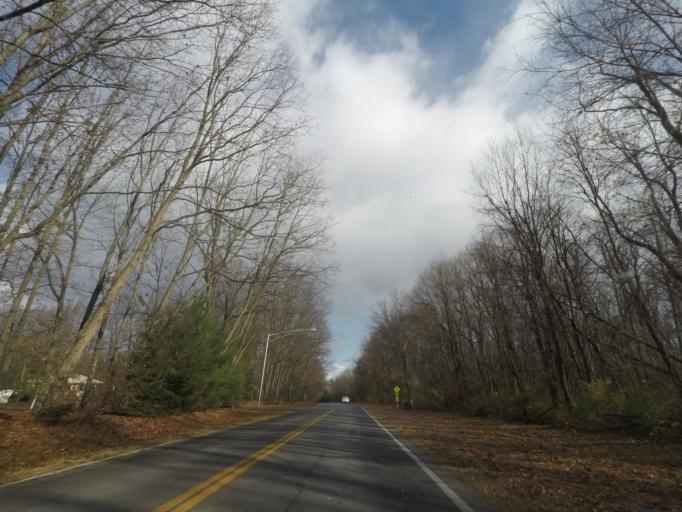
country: US
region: New York
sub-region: Saratoga County
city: Country Knolls
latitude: 42.8950
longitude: -73.7991
